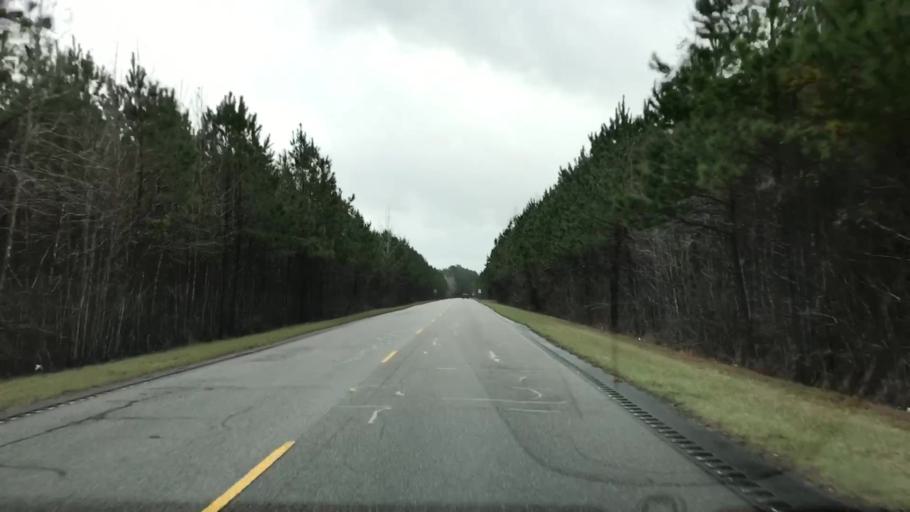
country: US
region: South Carolina
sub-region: Williamsburg County
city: Andrews
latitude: 33.5672
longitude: -79.4526
